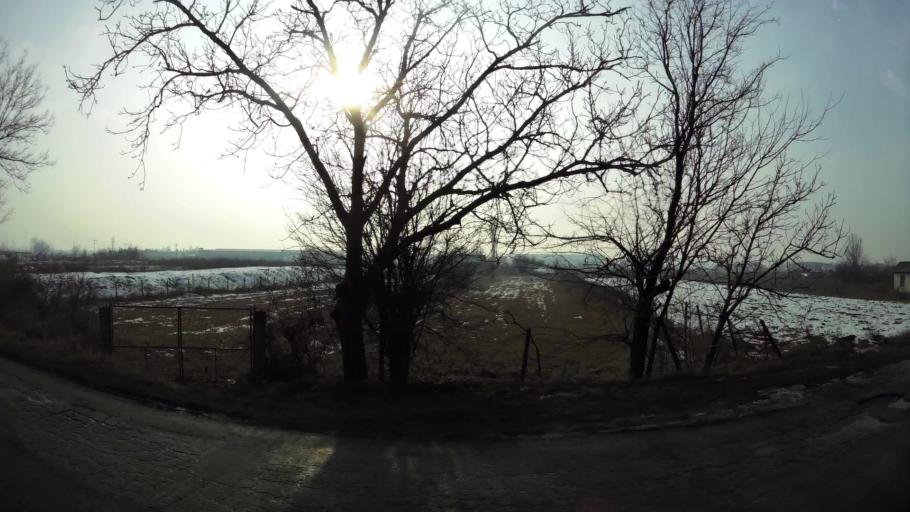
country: MK
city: Kadino
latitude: 41.9786
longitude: 21.5991
